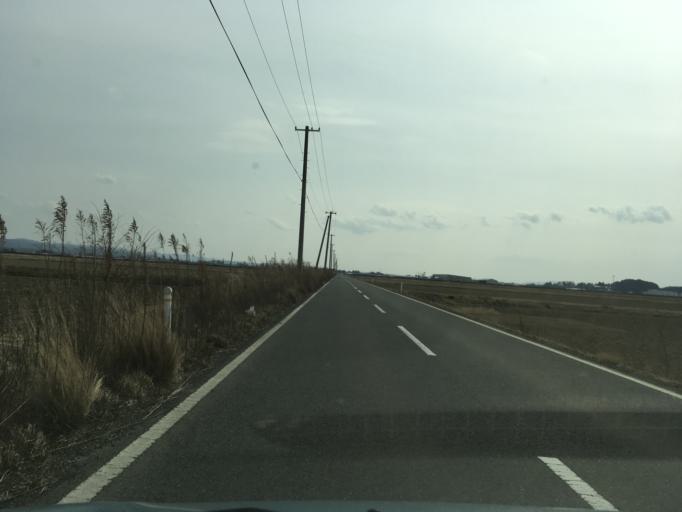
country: JP
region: Iwate
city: Ichinoseki
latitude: 38.7442
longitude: 141.2377
